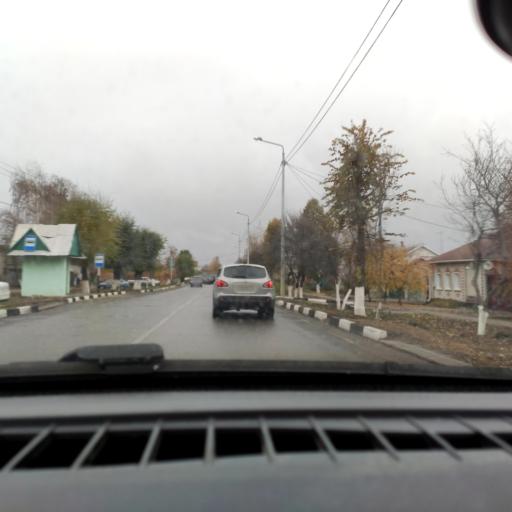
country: RU
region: Belgorod
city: Alekseyevka
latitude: 50.6327
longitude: 38.7015
